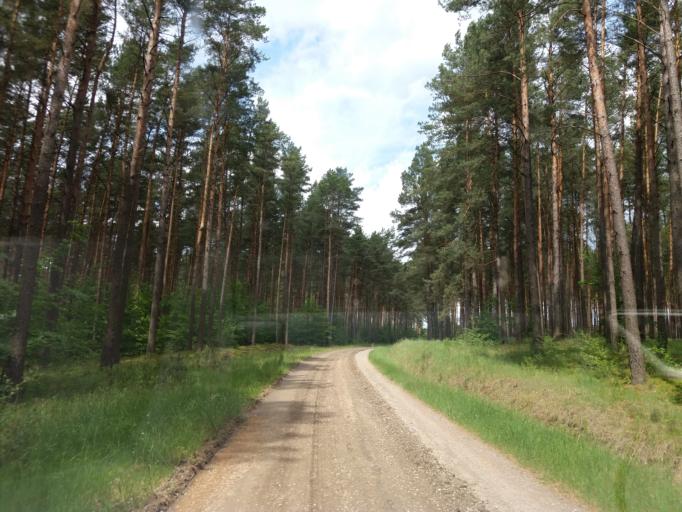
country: PL
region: West Pomeranian Voivodeship
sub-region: Powiat choszczenski
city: Drawno
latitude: 53.1984
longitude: 15.7181
